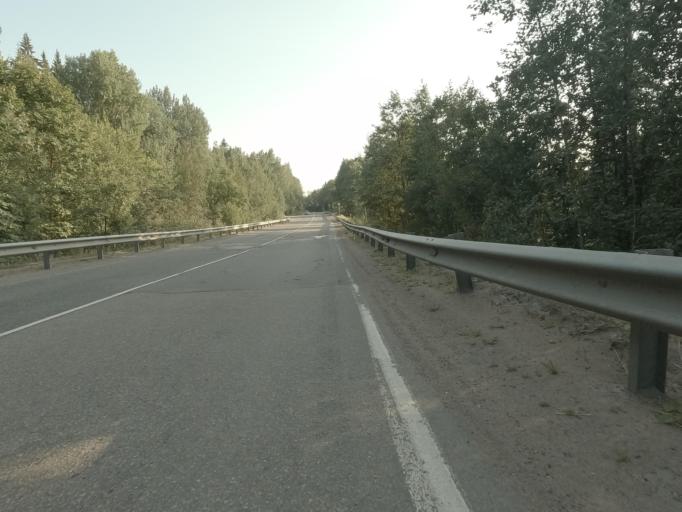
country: RU
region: Leningrad
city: Vyborg
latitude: 60.7407
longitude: 28.7637
